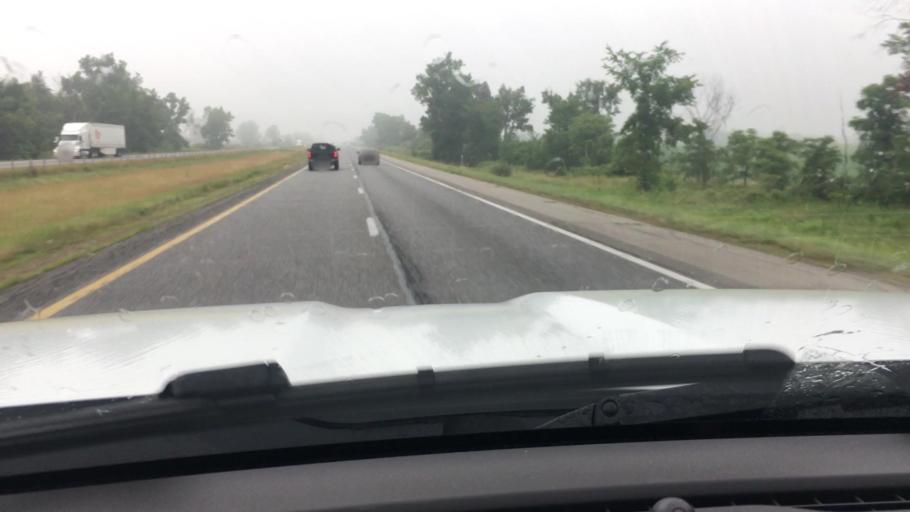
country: US
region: Michigan
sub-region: Shiawassee County
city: Corunna
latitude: 42.8993
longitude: -84.0790
